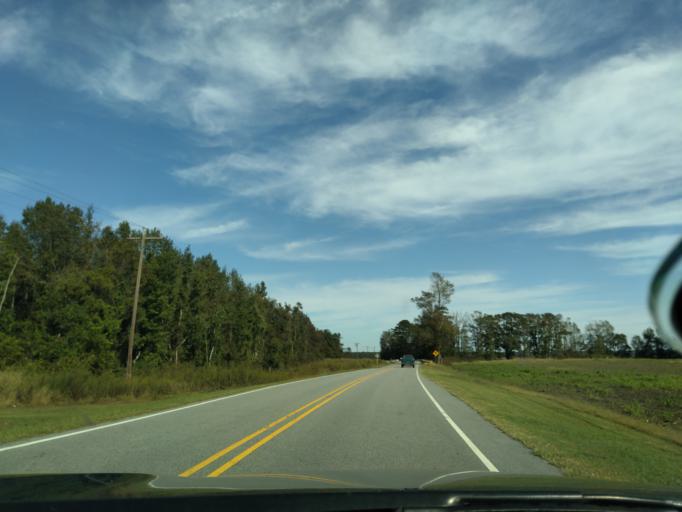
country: US
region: North Carolina
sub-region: Beaufort County
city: Belhaven
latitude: 35.6218
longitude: -76.6398
